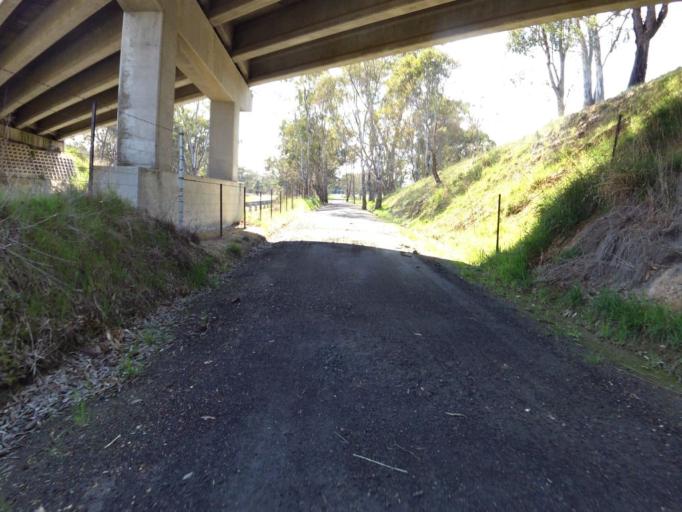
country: AU
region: Victoria
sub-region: Murrindindi
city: Alexandra
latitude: -37.1163
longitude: 145.6059
